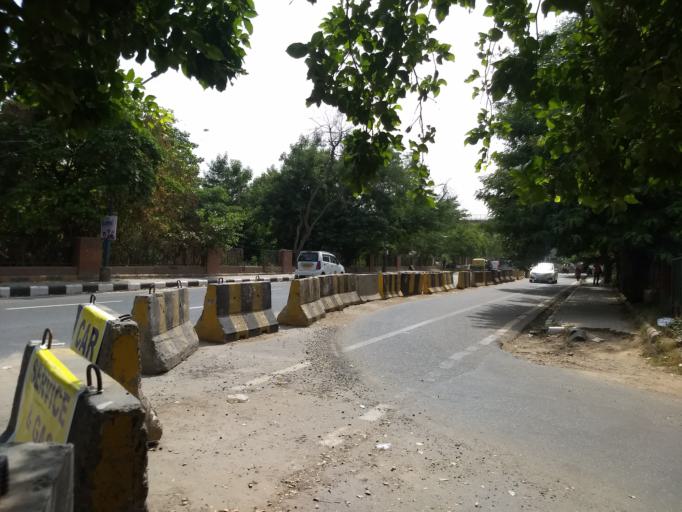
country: IN
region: Haryana
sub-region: Gurgaon
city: Gurgaon
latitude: 28.4680
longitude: 77.0744
